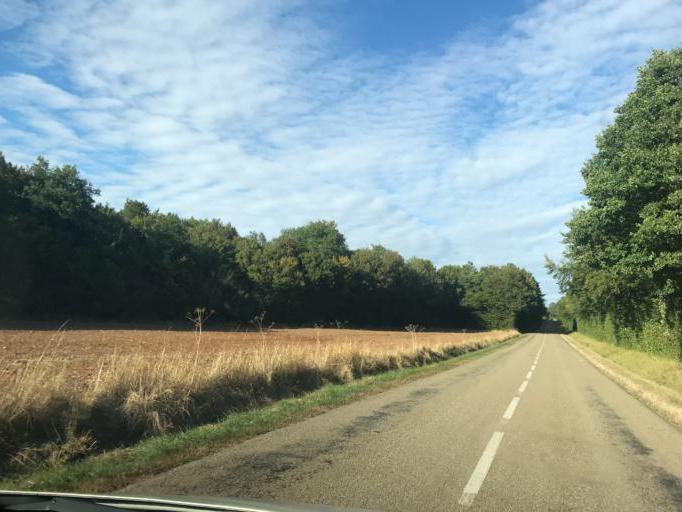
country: FR
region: Bourgogne
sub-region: Departement de l'Yonne
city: Fontenailles
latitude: 47.5662
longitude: 3.4452
